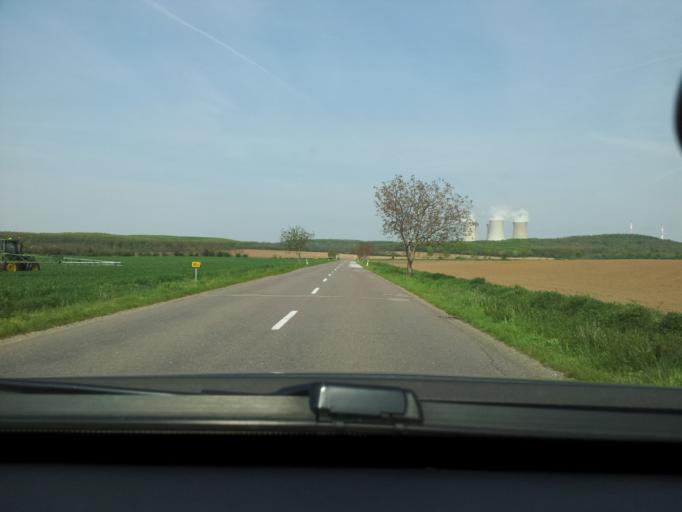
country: SK
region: Nitriansky
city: Tlmace
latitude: 48.2355
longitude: 18.4838
